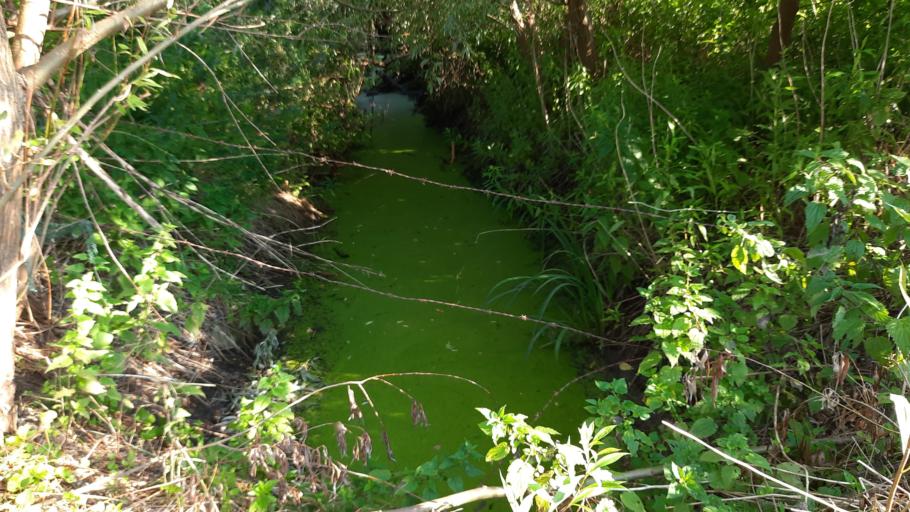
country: PL
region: Masovian Voivodeship
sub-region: Warszawa
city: Kabaty
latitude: 52.1337
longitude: 21.0831
